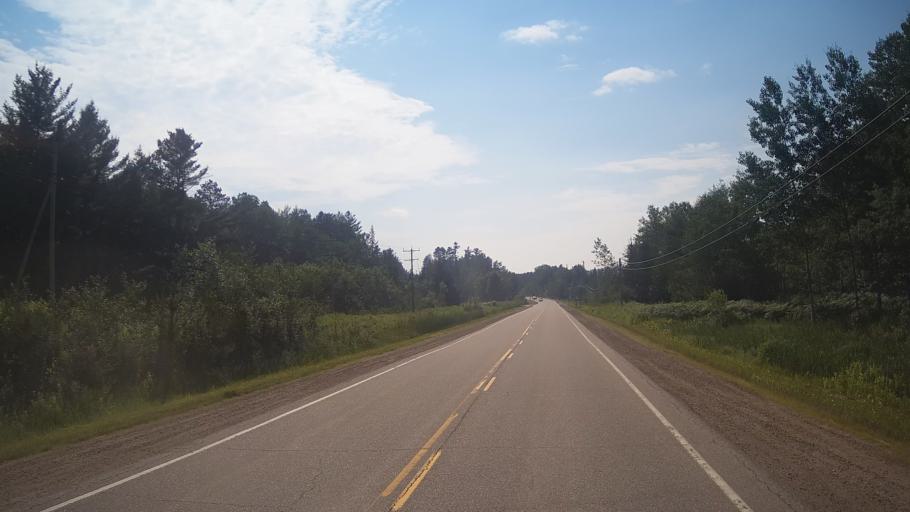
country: CA
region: Ontario
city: Petawawa
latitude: 45.5014
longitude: -77.6050
